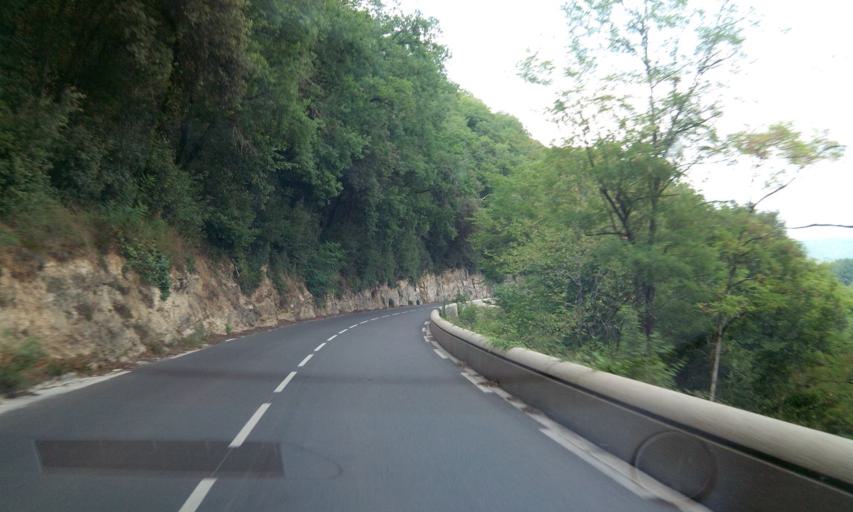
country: FR
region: Aquitaine
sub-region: Departement de la Dordogne
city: Eyvigues-et-Eybenes
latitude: 44.8616
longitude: 1.3496
